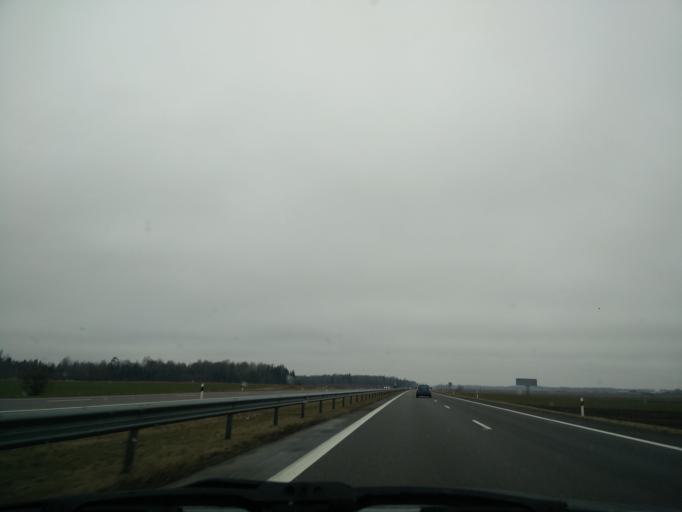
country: LT
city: Raseiniai
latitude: 55.3710
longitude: 22.9627
